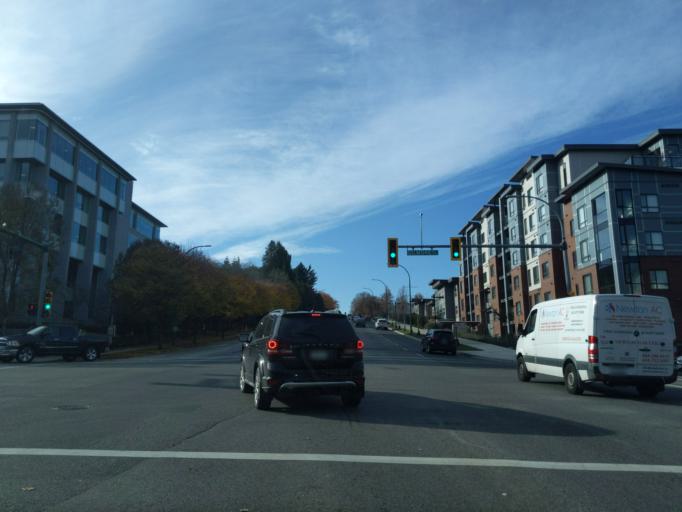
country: CA
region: British Columbia
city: Burnaby
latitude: 49.2547
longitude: -123.0104
